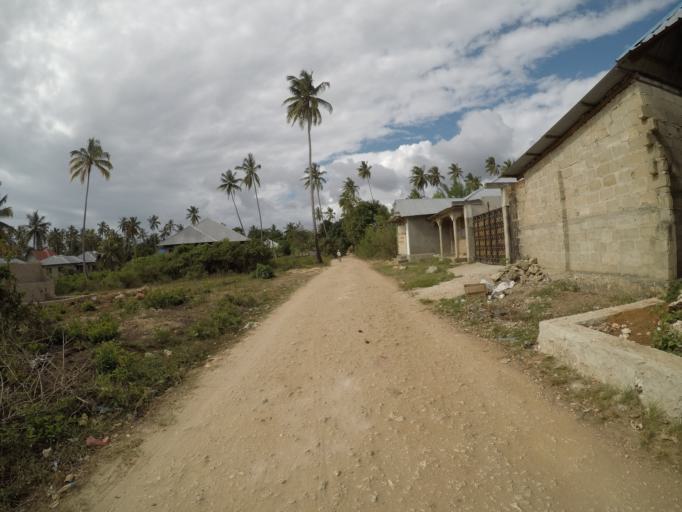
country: TZ
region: Zanzibar Central/South
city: Koani
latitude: -6.1904
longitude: 39.2640
